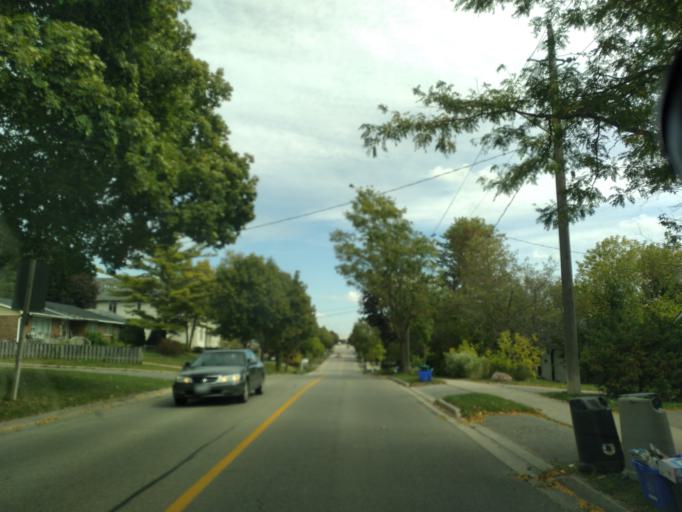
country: CA
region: Ontario
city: Newmarket
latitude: 44.0727
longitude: -79.4378
